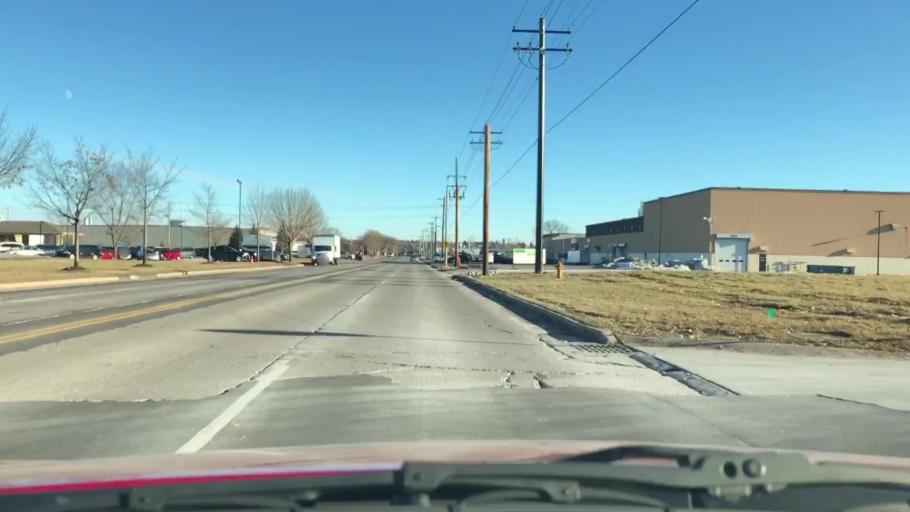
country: US
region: Wisconsin
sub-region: Brown County
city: Ashwaubenon
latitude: 44.4870
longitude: -88.0581
